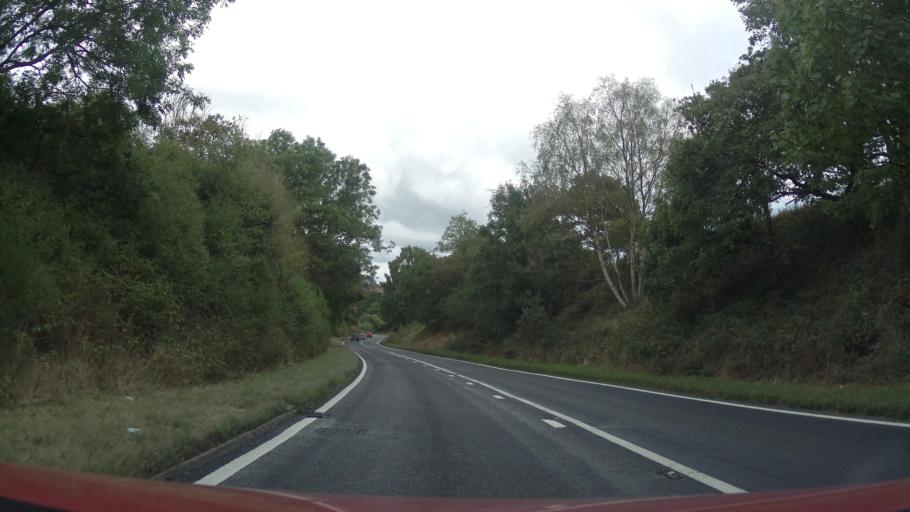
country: GB
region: England
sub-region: Shropshire
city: Bridgnorth
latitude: 52.5692
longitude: -2.3932
